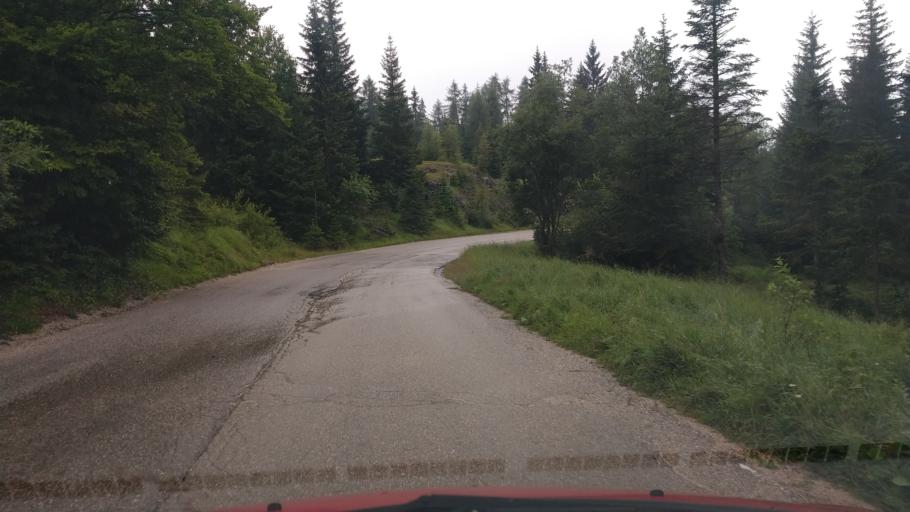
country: IT
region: Veneto
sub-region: Provincia di Vicenza
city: Lastebasse
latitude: 45.8934
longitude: 11.2669
